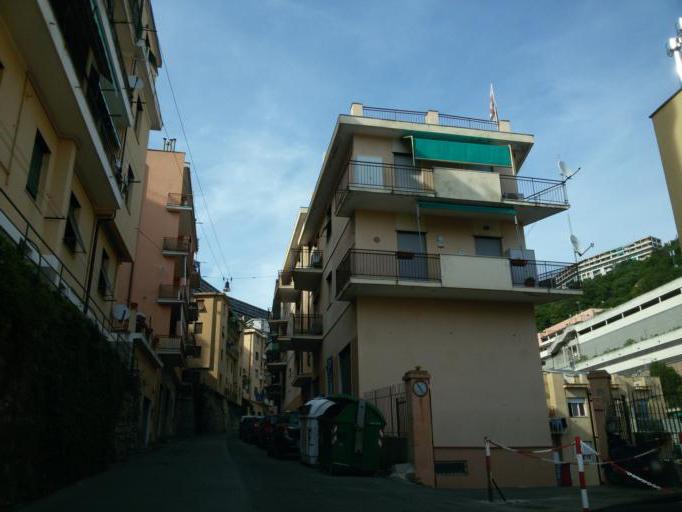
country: IT
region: Liguria
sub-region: Provincia di Genova
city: Genoa
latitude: 44.4203
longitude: 8.9569
